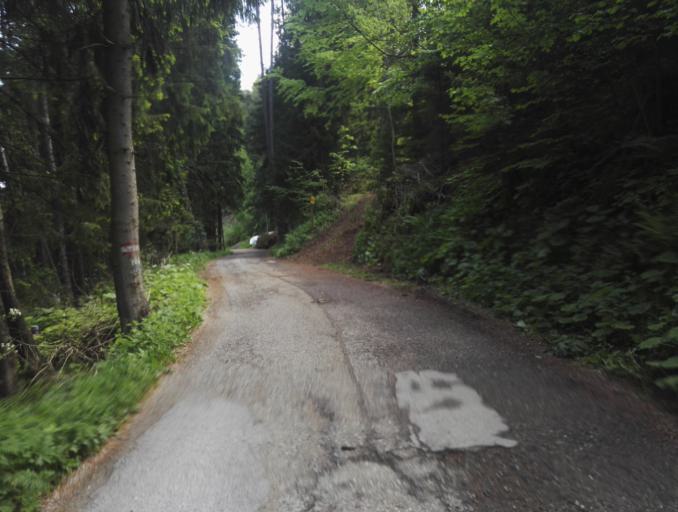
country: AT
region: Styria
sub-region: Politischer Bezirk Graz-Umgebung
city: Semriach
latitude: 47.1996
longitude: 15.4417
